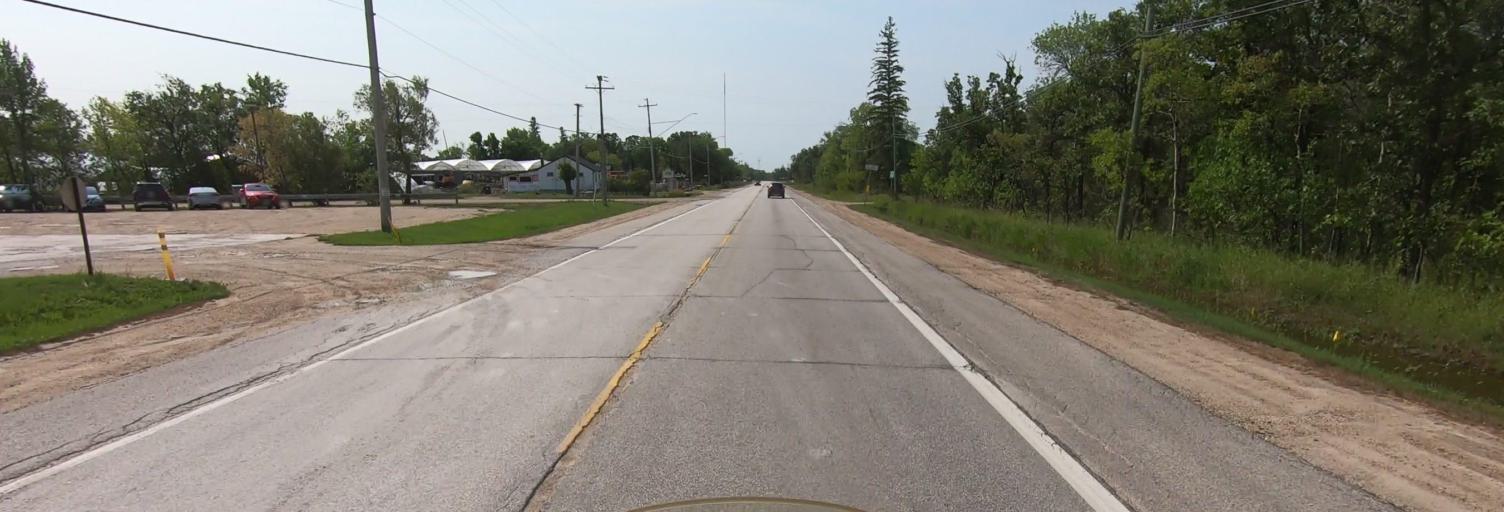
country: CA
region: Manitoba
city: Winnipeg
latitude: 49.7736
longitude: -97.1270
